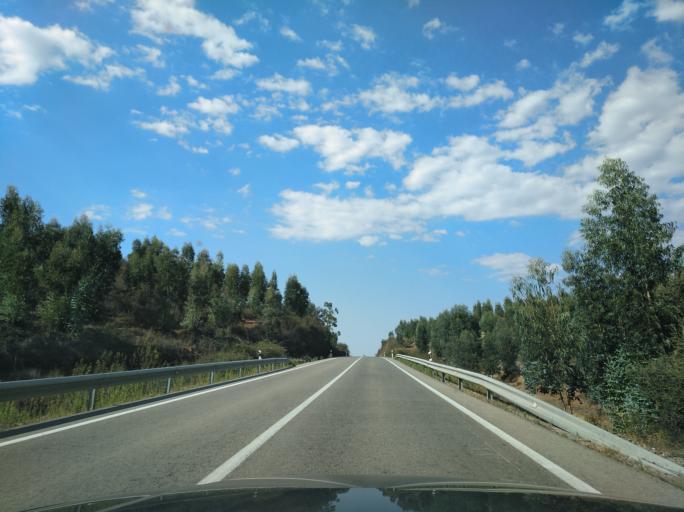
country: ES
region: Andalusia
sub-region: Provincia de Huelva
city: Santa Barbara de Casa
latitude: 37.8191
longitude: -7.2096
